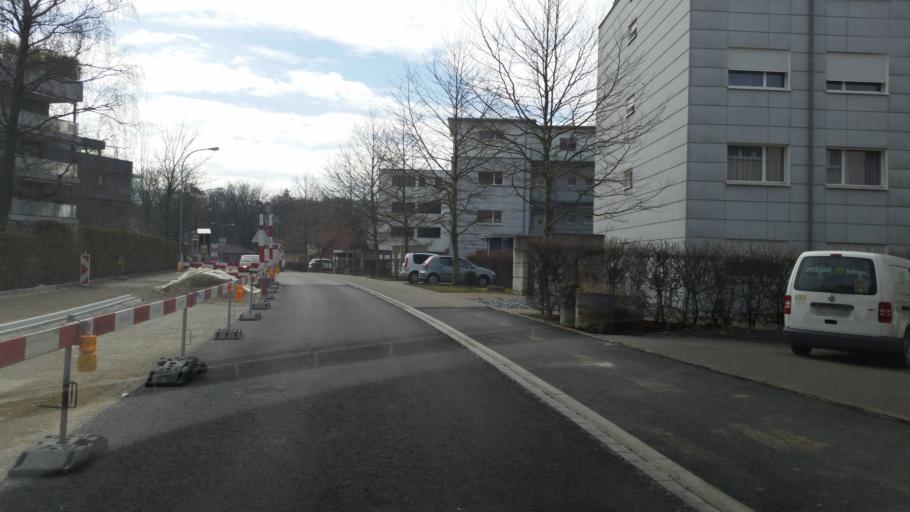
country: CH
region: Aargau
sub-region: Bezirk Baden
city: Neuenhof
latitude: 47.4577
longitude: 8.3342
